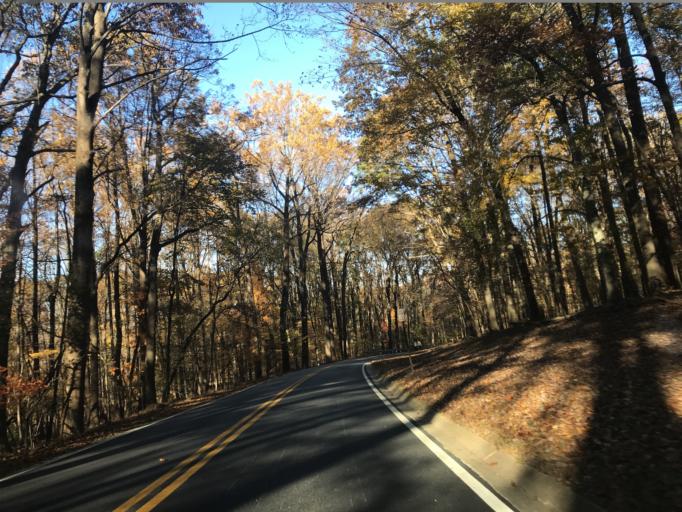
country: US
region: Maryland
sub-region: Baltimore County
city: Hampton
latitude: 39.4364
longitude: -76.5548
